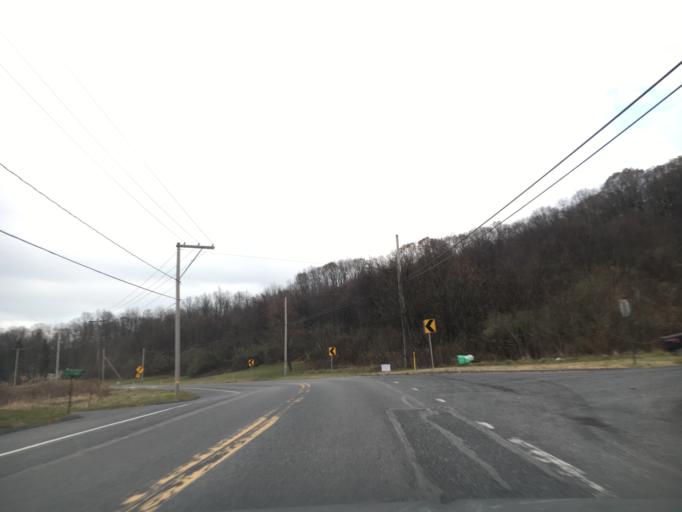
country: US
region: Pennsylvania
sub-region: Lehigh County
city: Slatington
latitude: 40.7222
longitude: -75.6134
